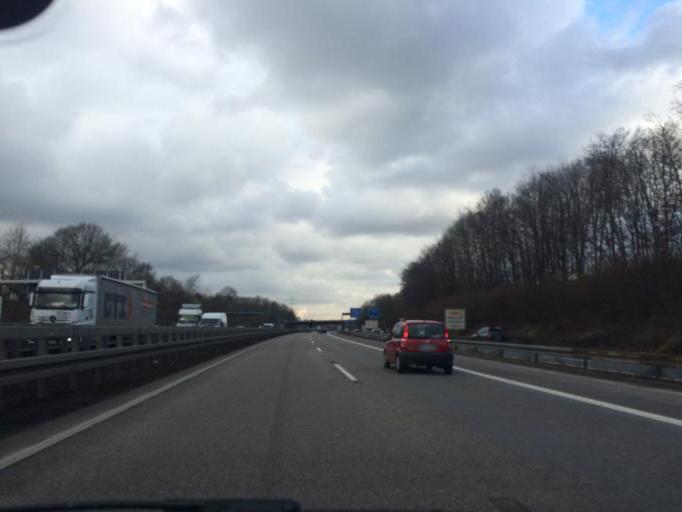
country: DE
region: North Rhine-Westphalia
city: Witten
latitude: 51.4568
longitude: 7.2889
